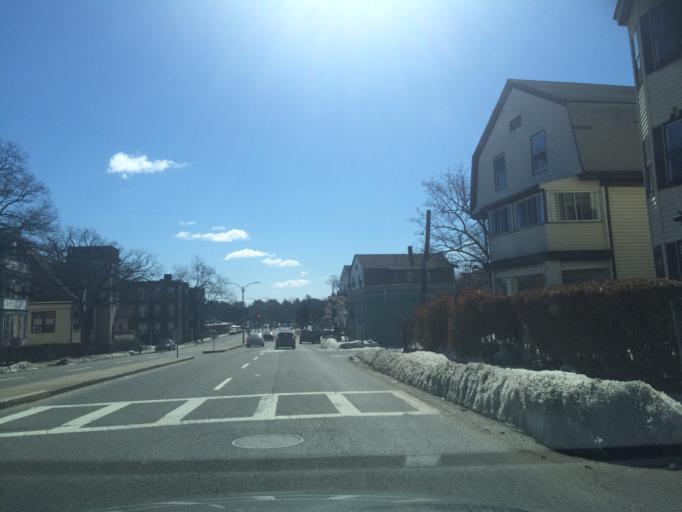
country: US
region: Massachusetts
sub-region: Norfolk County
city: Milton
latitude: 42.2696
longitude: -71.0972
